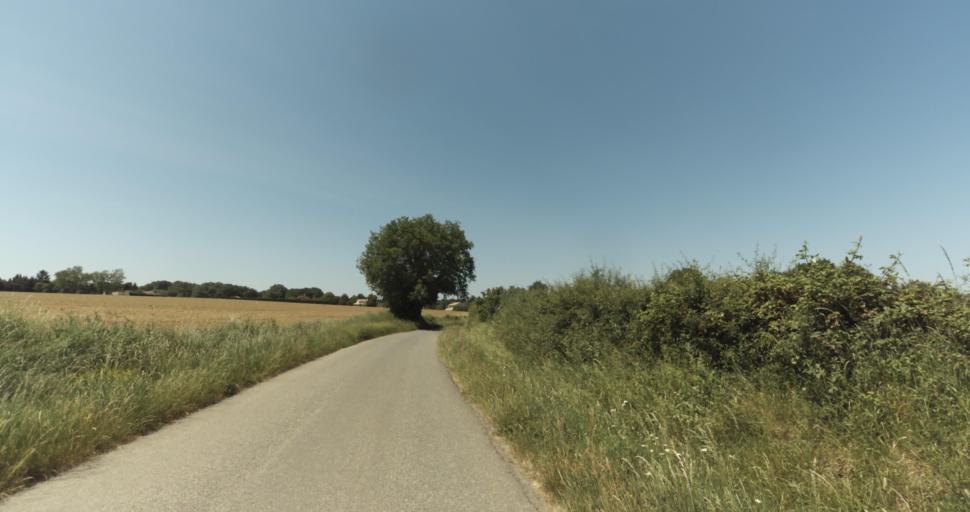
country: FR
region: Midi-Pyrenees
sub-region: Departement de la Haute-Garonne
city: Levignac
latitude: 43.6499
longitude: 1.1975
